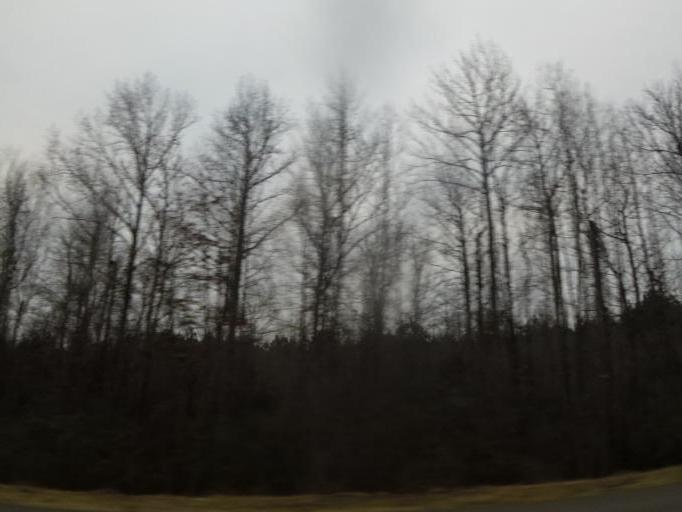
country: US
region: Alabama
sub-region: Blount County
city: Smoke Rise
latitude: 33.8513
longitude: -86.8286
